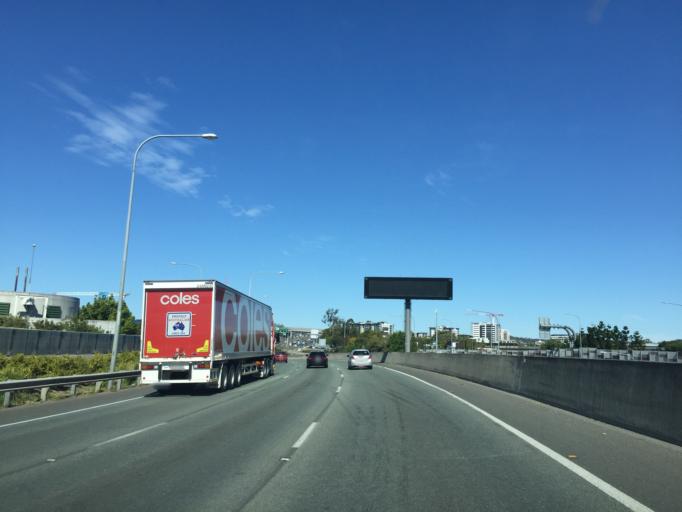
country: AU
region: Queensland
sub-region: Brisbane
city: Woolloongabba
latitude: -27.4915
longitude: 153.0338
